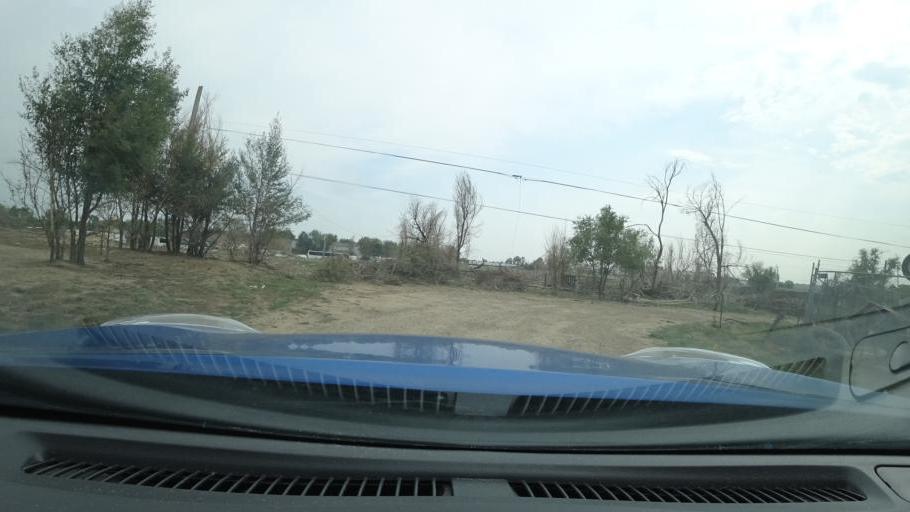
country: US
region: Colorado
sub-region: Adams County
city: Aurora
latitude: 39.7519
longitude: -104.7706
